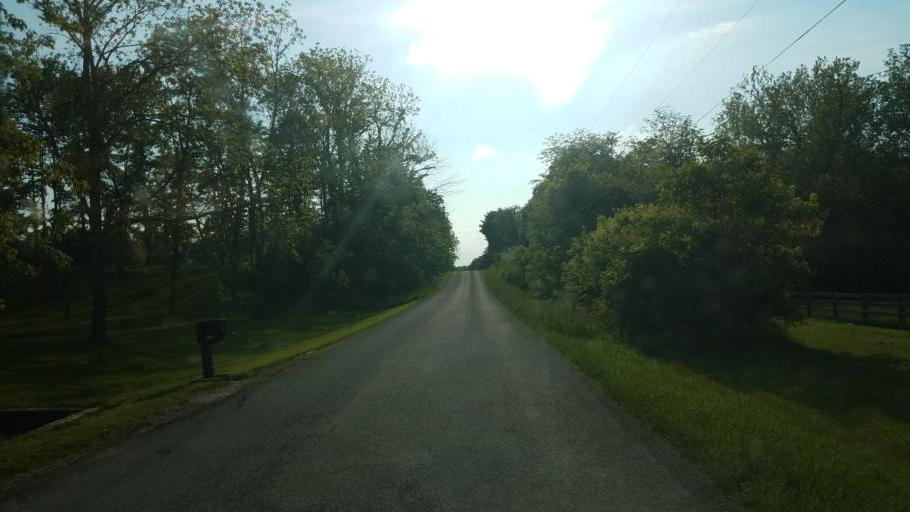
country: US
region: Ohio
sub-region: Knox County
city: Centerburg
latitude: 40.3926
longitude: -82.7922
